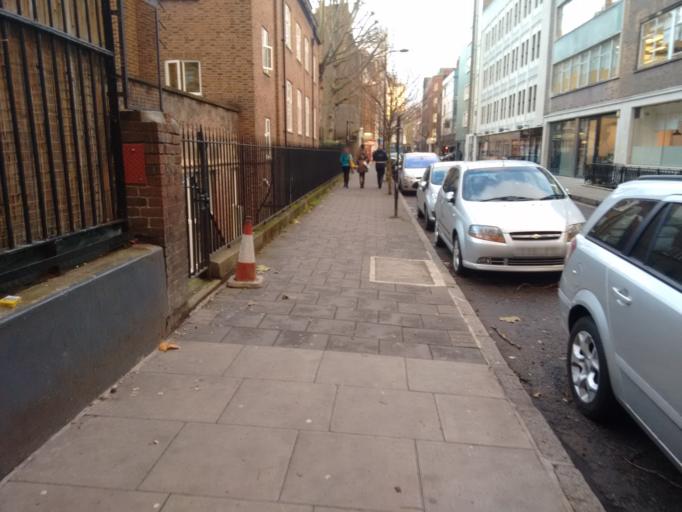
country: GB
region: England
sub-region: Greater London
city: London
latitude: 51.5211
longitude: -0.1360
